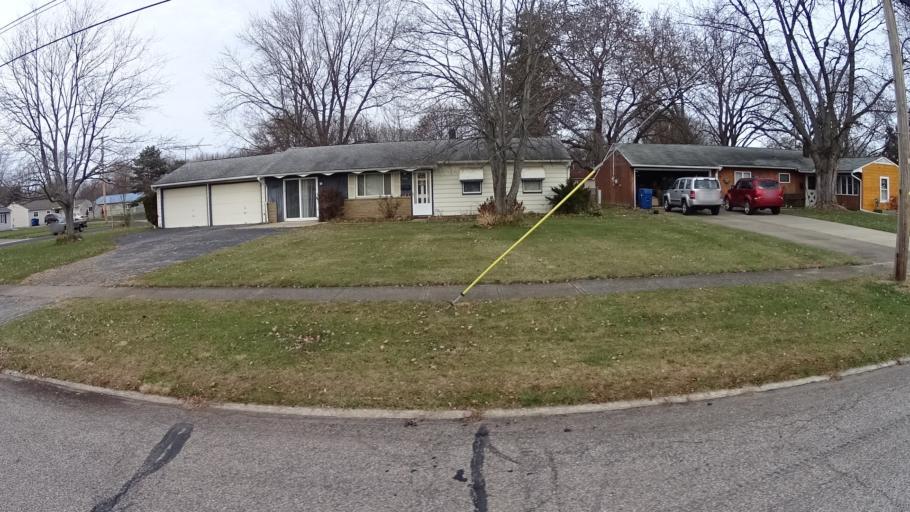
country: US
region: Ohio
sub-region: Lorain County
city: North Ridgeville
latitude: 41.3840
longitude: -81.9934
